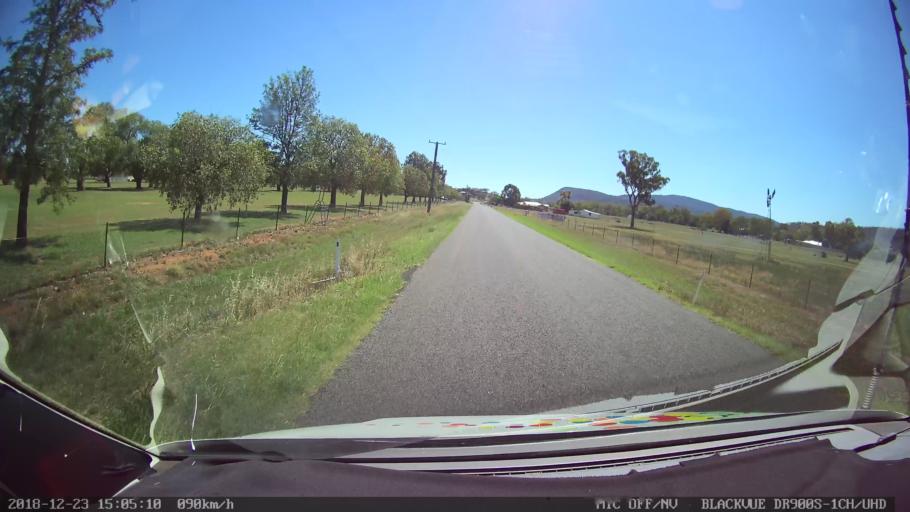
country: AU
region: New South Wales
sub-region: Tamworth Municipality
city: Manilla
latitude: -30.7427
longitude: 150.7419
